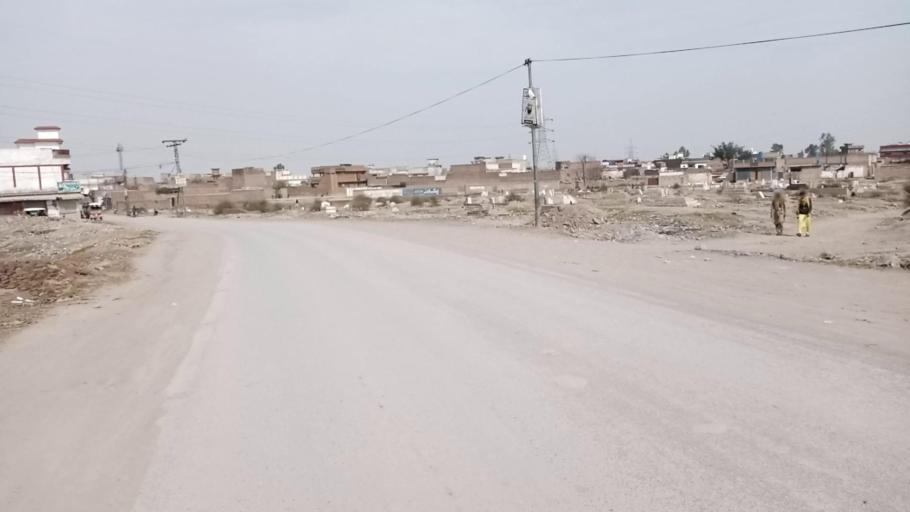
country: PK
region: Khyber Pakhtunkhwa
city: Peshawar
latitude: 33.9855
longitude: 71.4681
